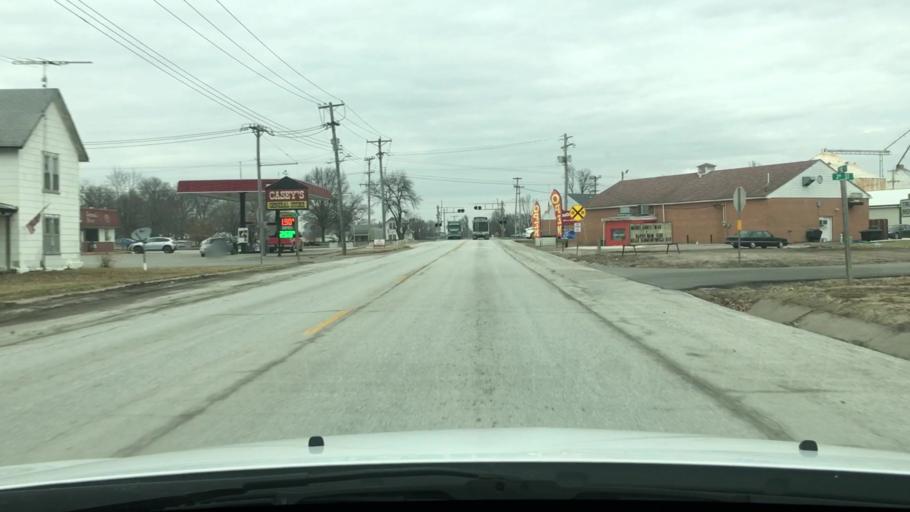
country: US
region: Missouri
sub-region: Audrain County
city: Vandalia
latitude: 39.2409
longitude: -91.6456
